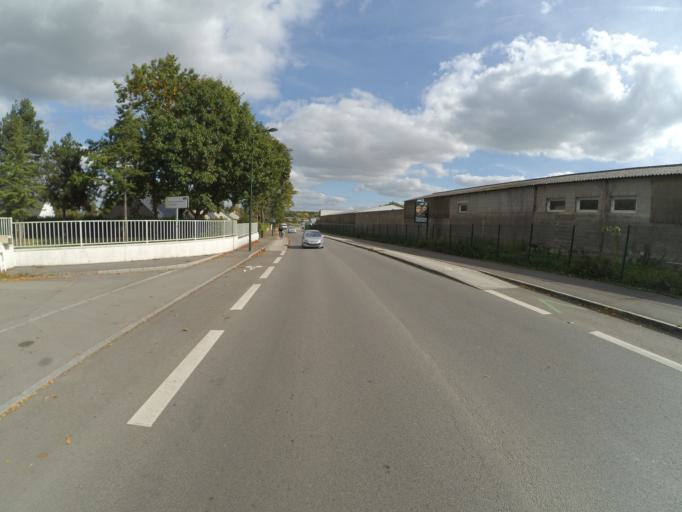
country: FR
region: Pays de la Loire
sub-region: Departement de la Loire-Atlantique
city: Carquefou
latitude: 47.2956
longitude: -1.4814
